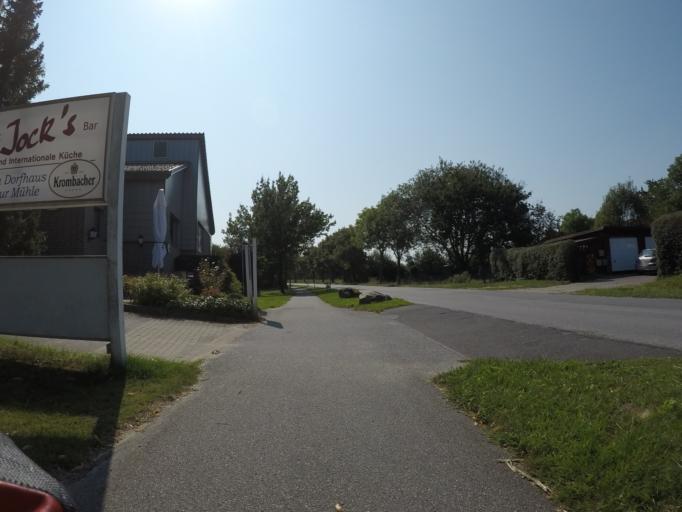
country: DE
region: Schleswig-Holstein
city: Sievershutten
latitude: 53.8437
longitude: 10.1096
